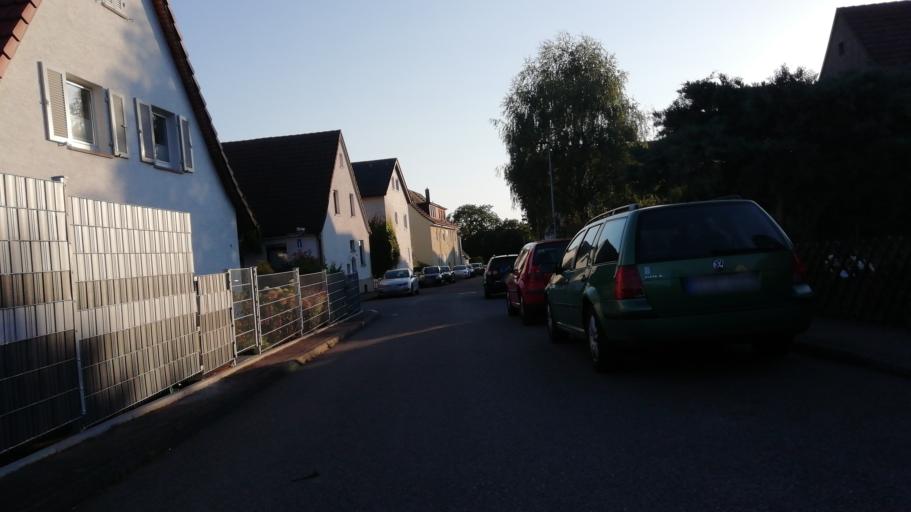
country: DE
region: Baden-Wuerttemberg
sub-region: Regierungsbezirk Stuttgart
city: Korntal
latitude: 48.8172
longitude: 9.1176
